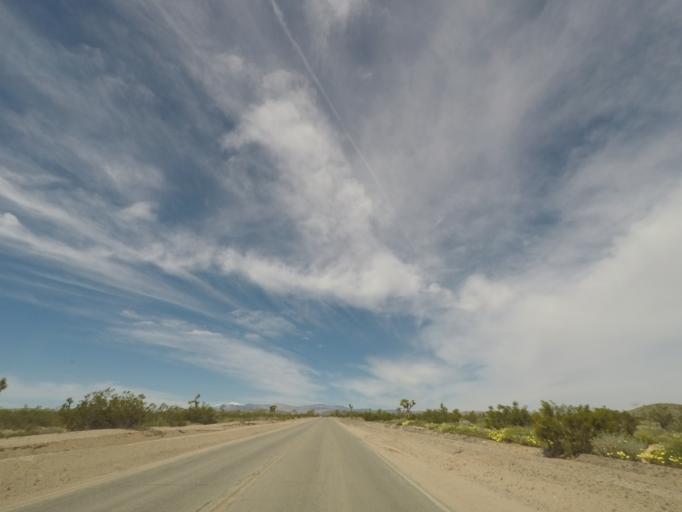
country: US
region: California
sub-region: San Bernardino County
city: Joshua Tree
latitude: 34.1930
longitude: -116.3433
